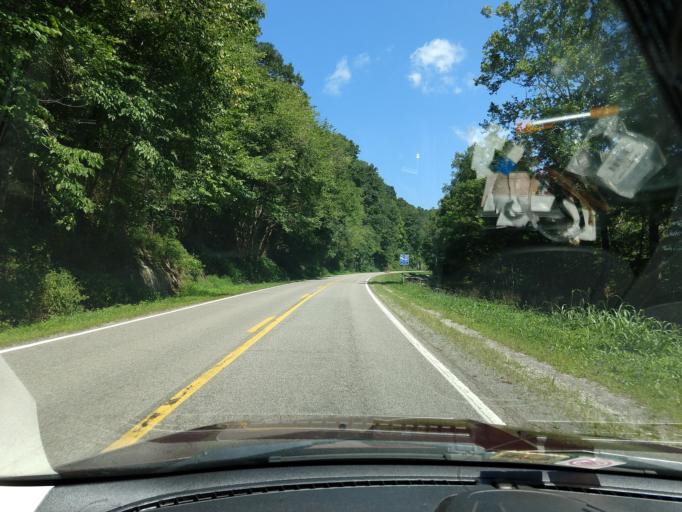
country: US
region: West Virginia
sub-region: Kanawha County
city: Montgomery
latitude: 38.1316
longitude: -81.2205
